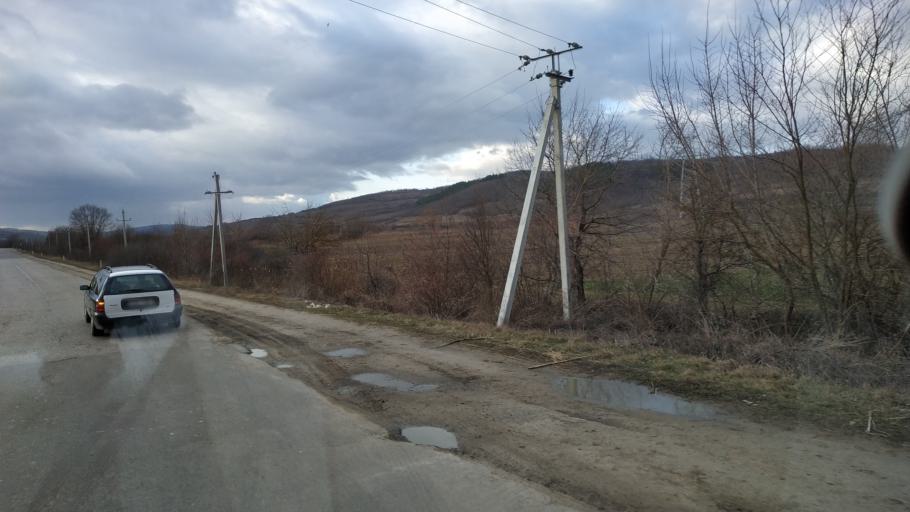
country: MD
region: Calarasi
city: Calarasi
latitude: 47.3105
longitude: 28.3797
